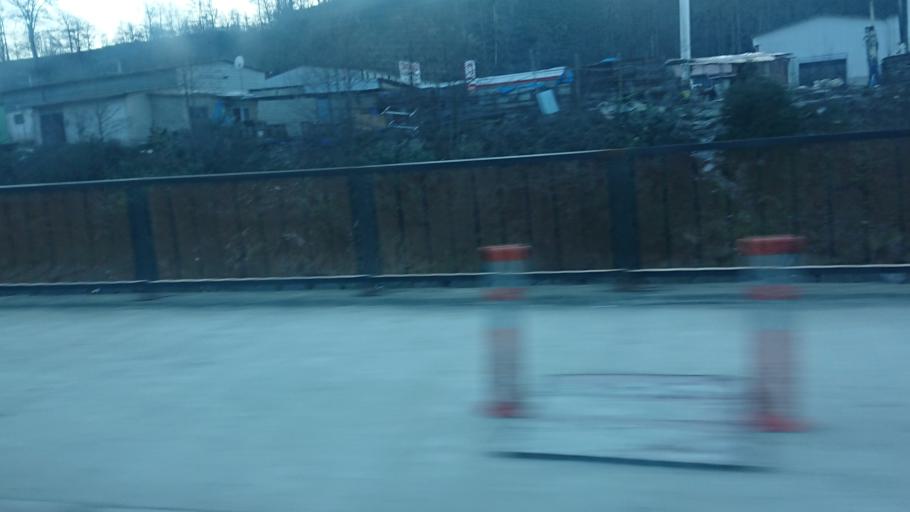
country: TR
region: Rize
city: Gundogdu
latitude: 41.0313
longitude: 40.5833
